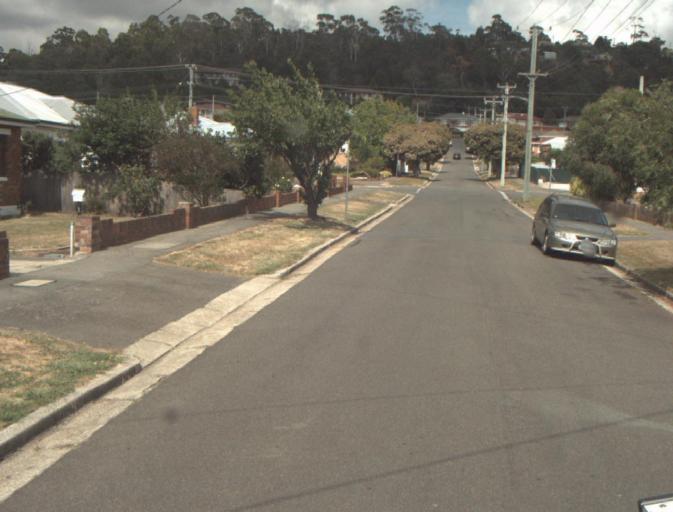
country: AU
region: Tasmania
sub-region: Launceston
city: Summerhill
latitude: -41.4699
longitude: 147.1572
